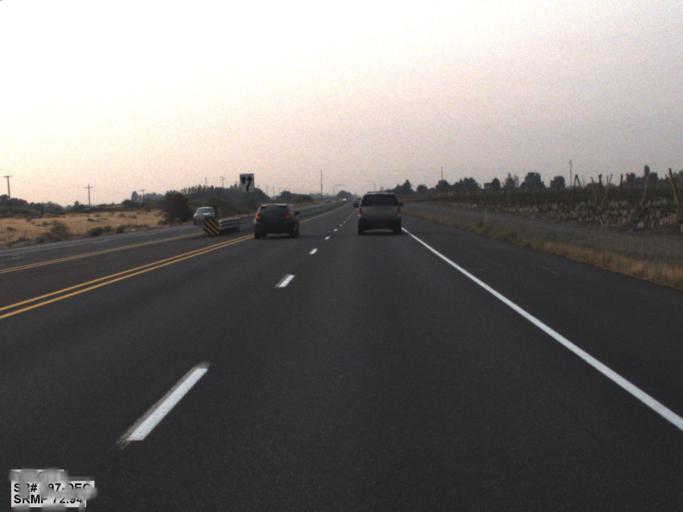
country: US
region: Washington
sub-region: Yakima County
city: Union Gap
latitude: 46.4980
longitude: -120.4629
